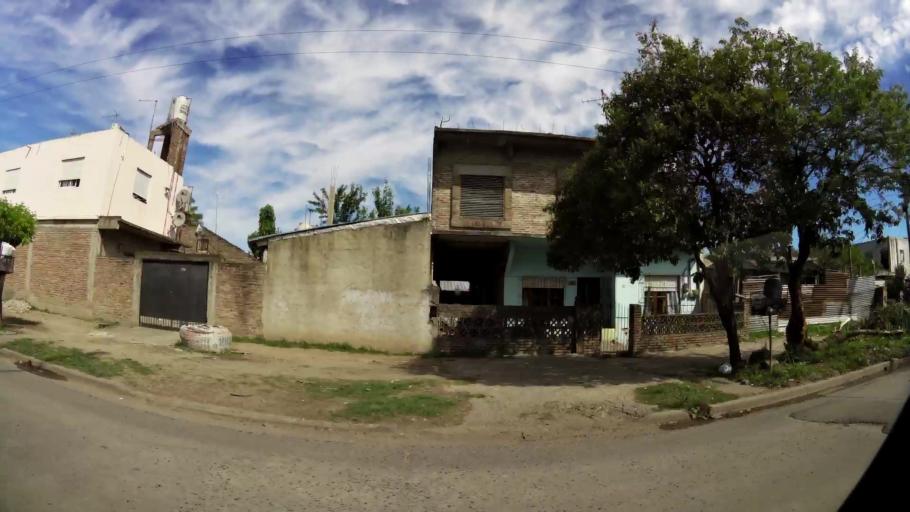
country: AR
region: Buenos Aires
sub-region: Partido de Quilmes
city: Quilmes
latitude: -34.7789
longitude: -58.3006
